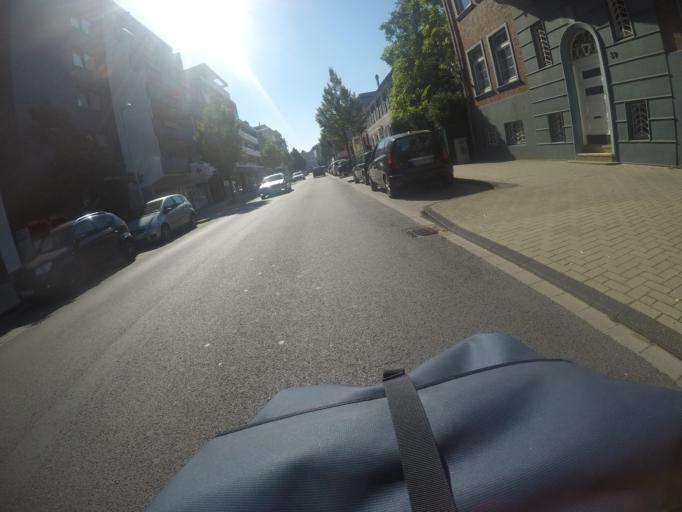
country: DE
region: North Rhine-Westphalia
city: Opladen
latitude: 51.0694
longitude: 7.0005
